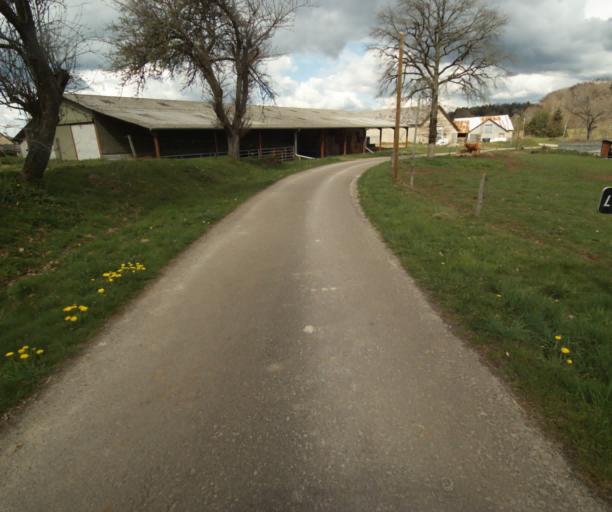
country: FR
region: Limousin
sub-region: Departement de la Correze
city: Correze
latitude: 45.2554
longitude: 1.9034
